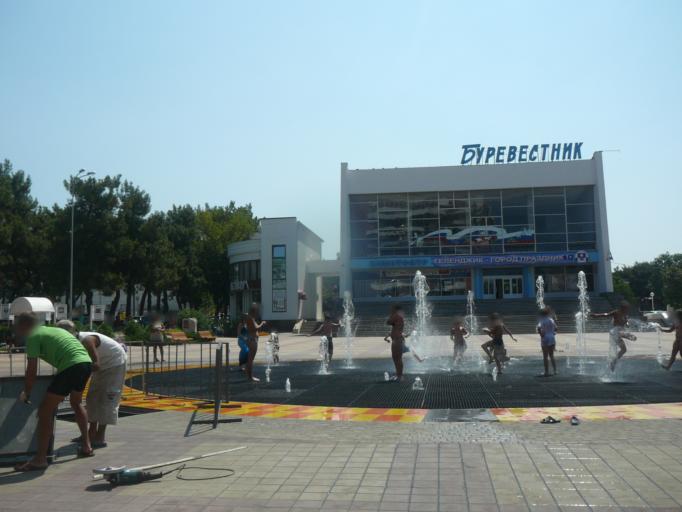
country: RU
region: Krasnodarskiy
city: Gelendzhik
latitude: 44.5630
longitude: 38.0789
